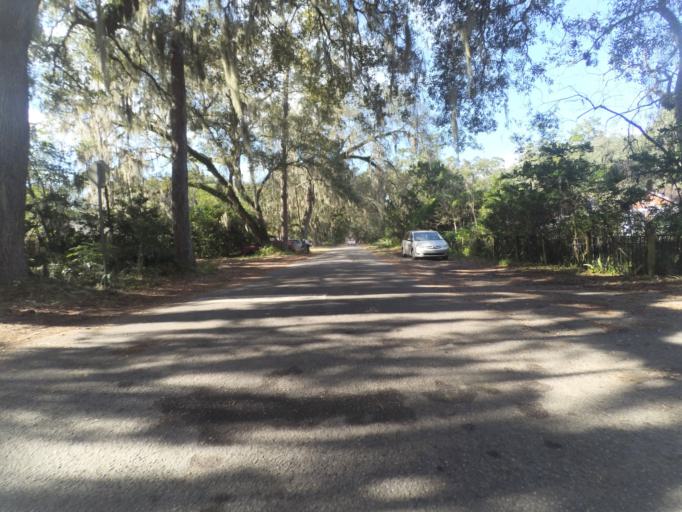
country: US
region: Florida
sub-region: Alachua County
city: Gainesville
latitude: 29.6649
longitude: -82.3350
